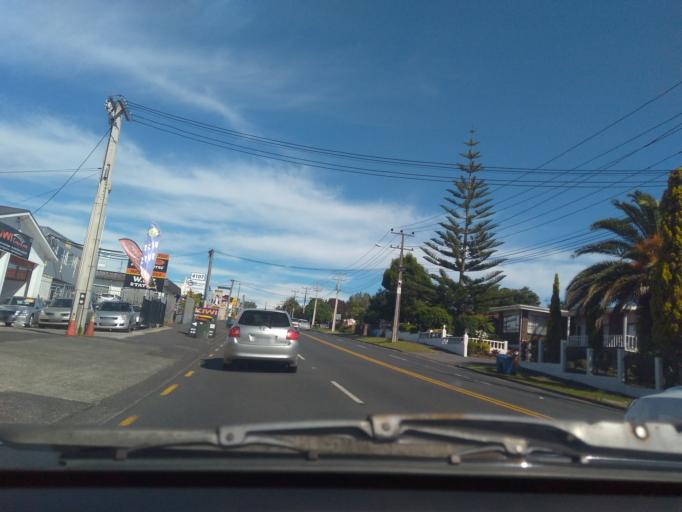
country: NZ
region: Auckland
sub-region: Auckland
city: Waitakere
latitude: -36.9029
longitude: 174.6568
